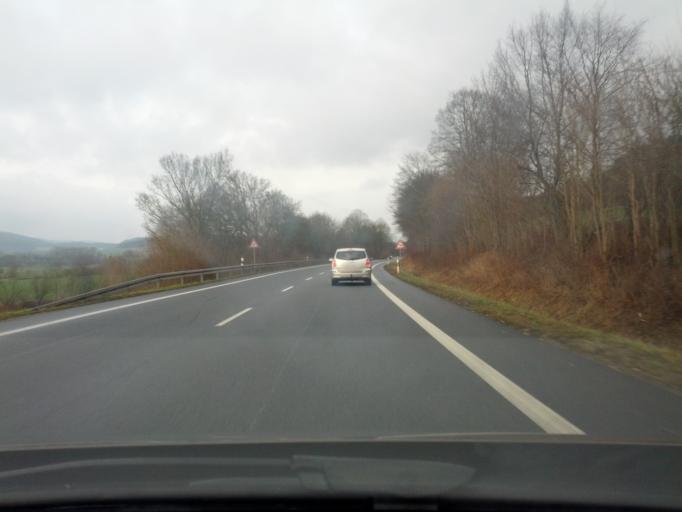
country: DE
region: Hesse
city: Witzenhausen
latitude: 51.3666
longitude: 9.8150
